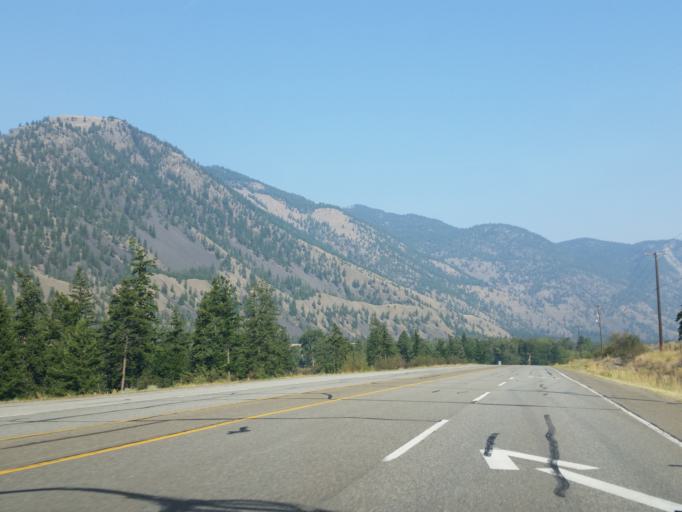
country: CA
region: British Columbia
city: Oliver
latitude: 49.2513
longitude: -120.0098
